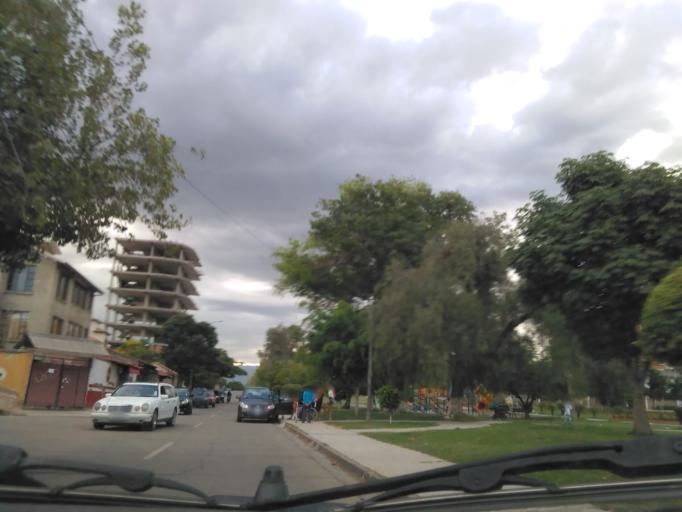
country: BO
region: Cochabamba
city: Cochabamba
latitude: -17.3703
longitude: -66.1695
